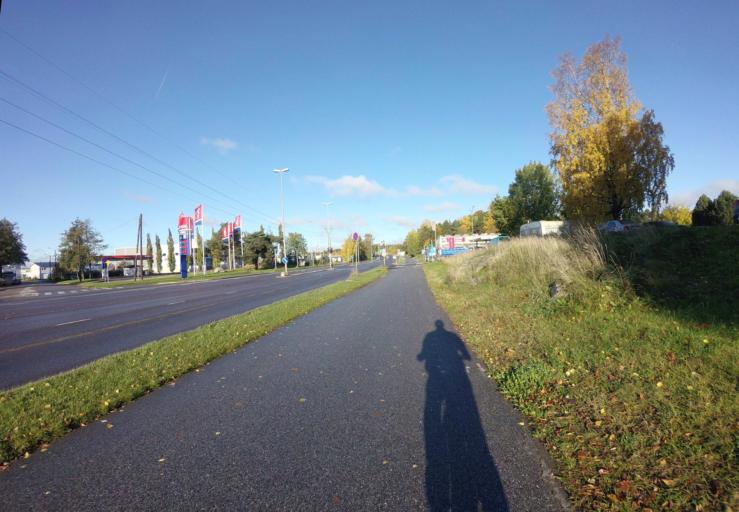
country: FI
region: Varsinais-Suomi
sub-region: Turku
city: Turku
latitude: 60.4459
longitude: 22.2220
